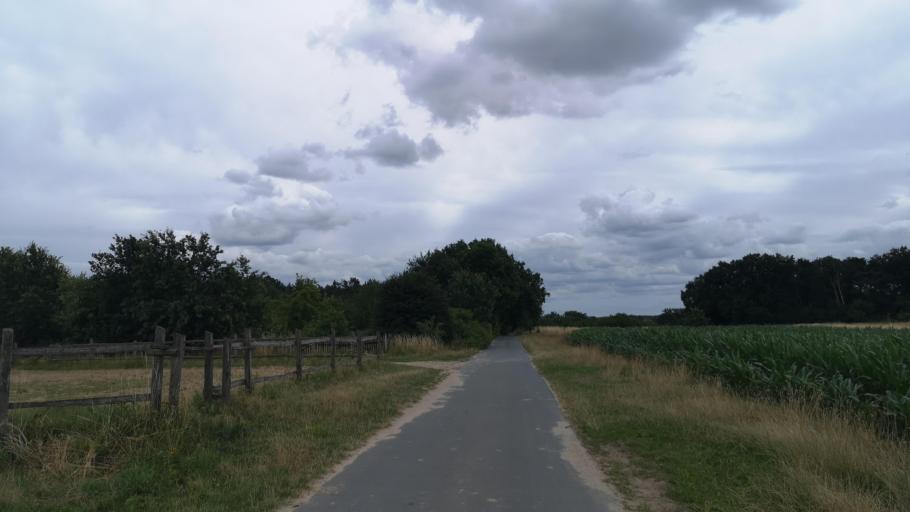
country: DE
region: Lower Saxony
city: Thomasburg
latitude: 53.2285
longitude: 10.6990
